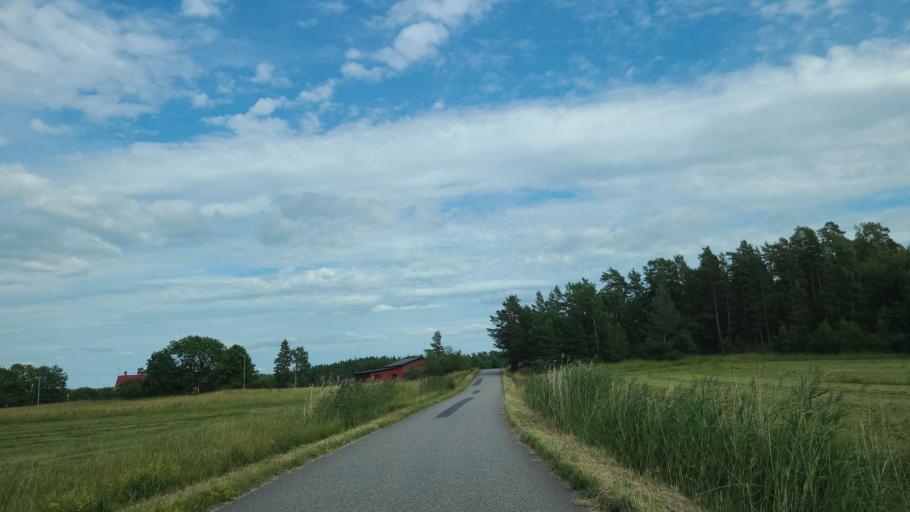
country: FI
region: Varsinais-Suomi
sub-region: Turku
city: Rymaettylae
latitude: 60.2905
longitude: 21.9563
